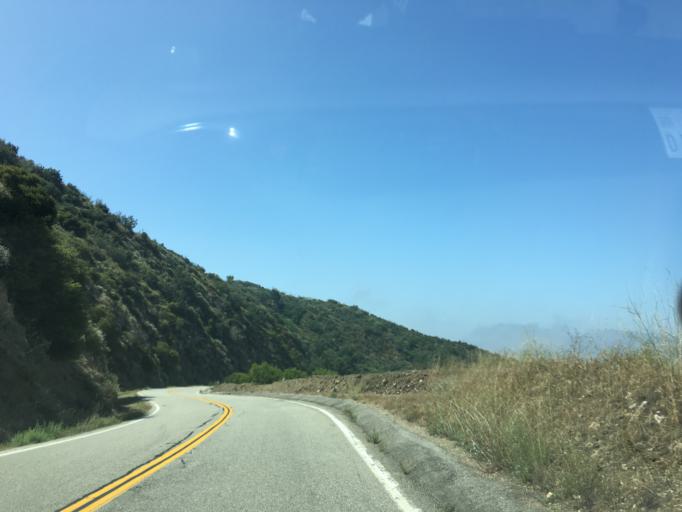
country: US
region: California
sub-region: Los Angeles County
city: Glendora
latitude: 34.1901
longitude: -117.8414
